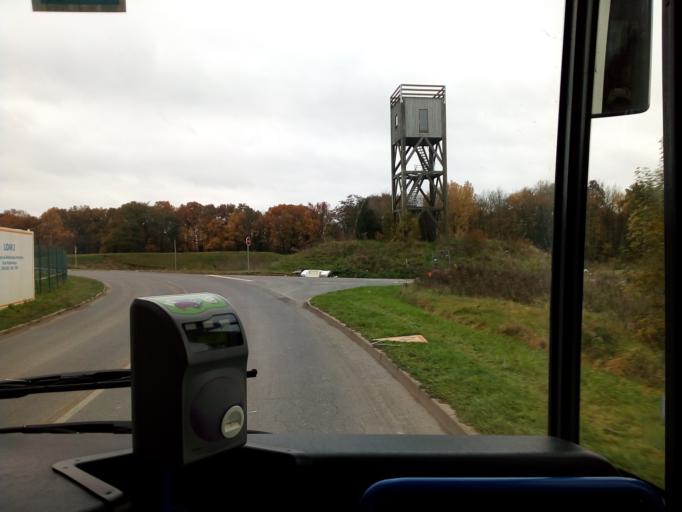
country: FR
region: Ile-de-France
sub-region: Departement de l'Essonne
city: Vauhallan
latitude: 48.7111
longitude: 2.2048
